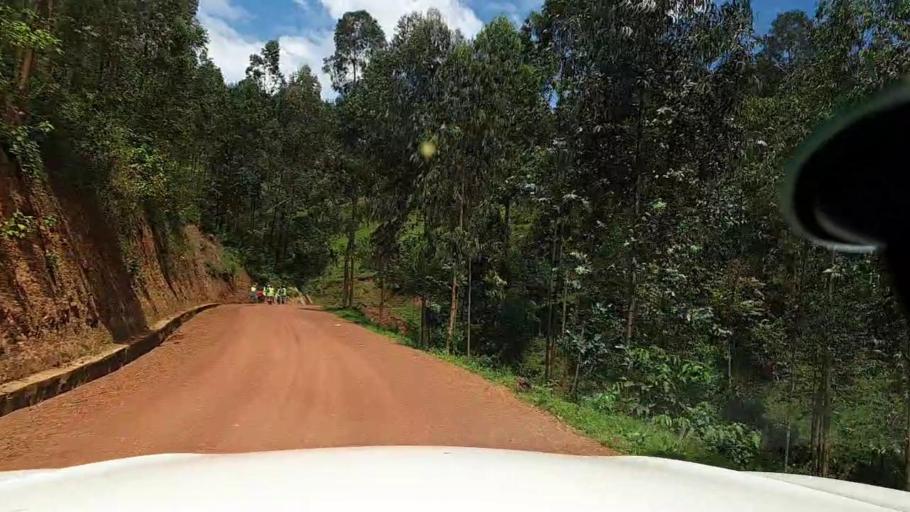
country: RW
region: Northern Province
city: Byumba
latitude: -1.7401
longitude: 29.8611
